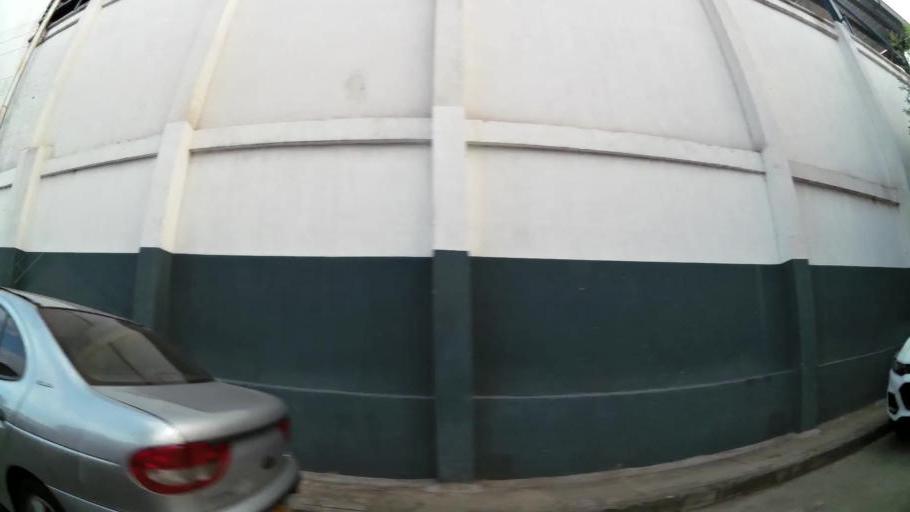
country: CO
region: Valle del Cauca
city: Cali
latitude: 3.4624
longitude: -76.5121
